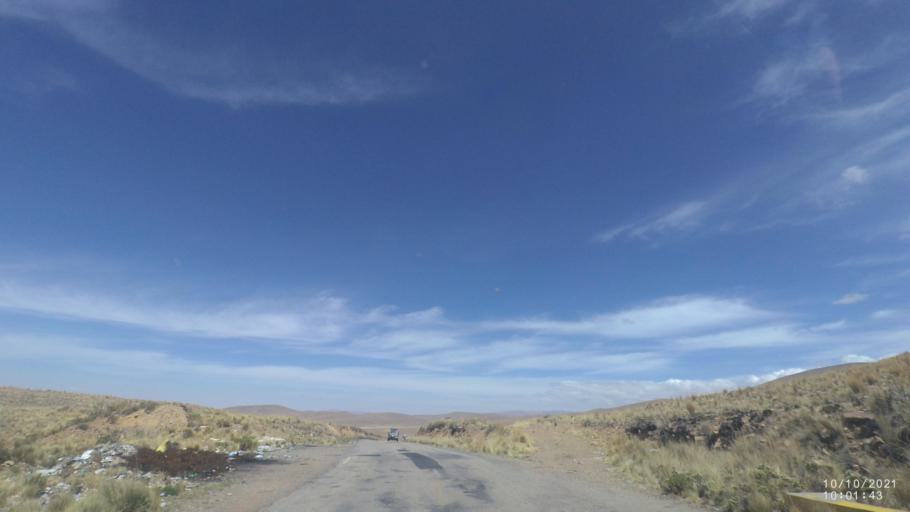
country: BO
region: La Paz
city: Eucaliptus
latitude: -17.3643
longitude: -67.4249
